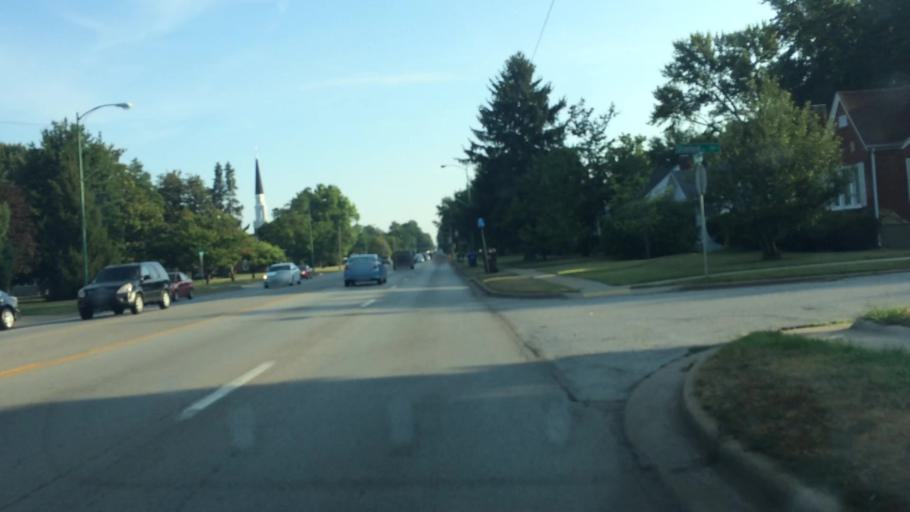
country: US
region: Missouri
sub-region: Greene County
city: Springfield
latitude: 37.1837
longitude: -93.2765
